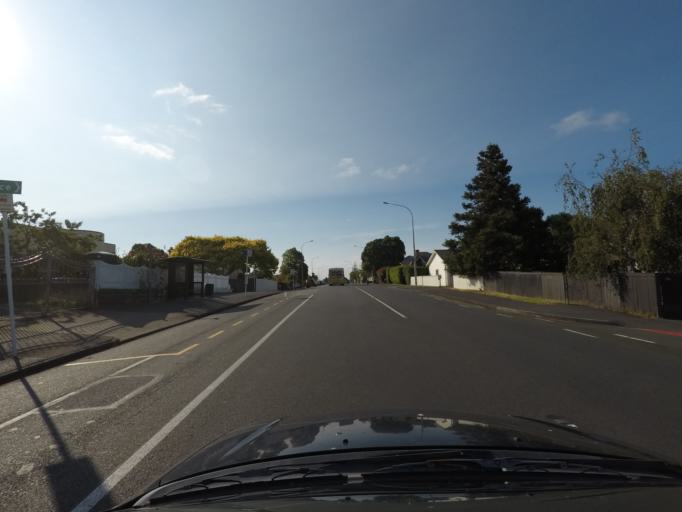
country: NZ
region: Auckland
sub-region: Auckland
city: Rosebank
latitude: -36.8828
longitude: 174.7138
